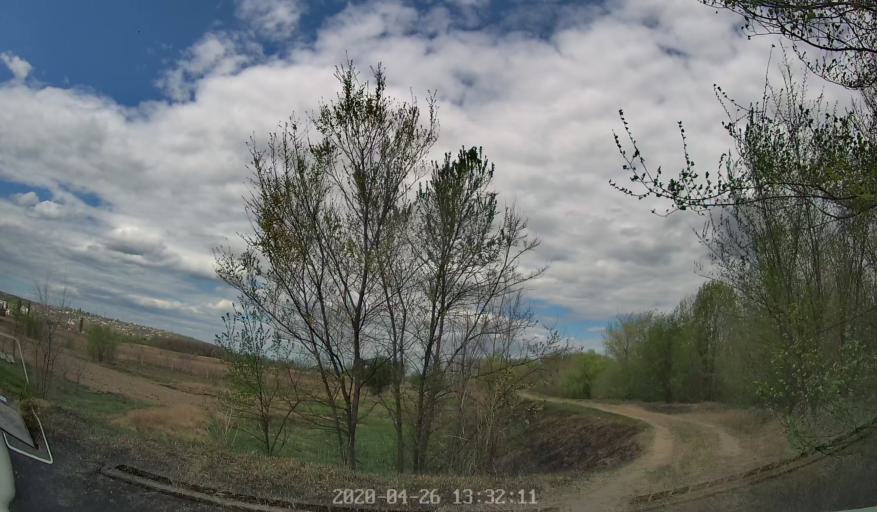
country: MD
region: Criuleni
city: Criuleni
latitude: 47.2086
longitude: 29.1776
